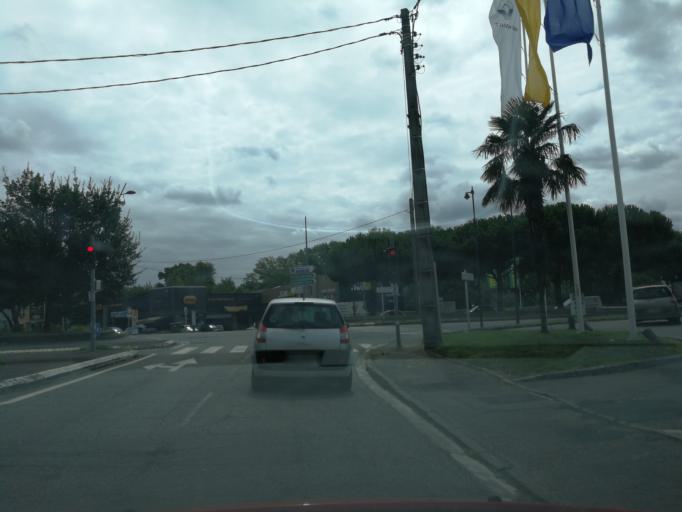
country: FR
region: Midi-Pyrenees
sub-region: Departement de la Haute-Garonne
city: Ramonville-Saint-Agne
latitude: 43.5716
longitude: 1.4986
